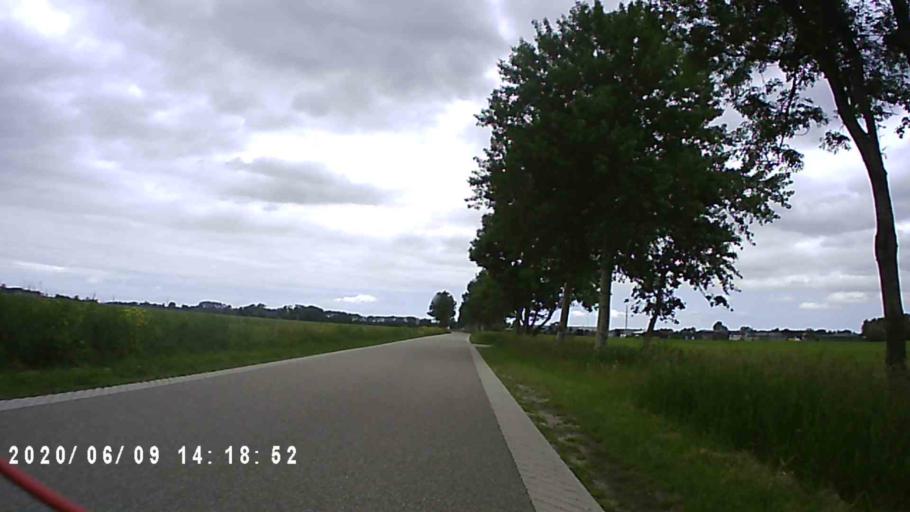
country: NL
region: Groningen
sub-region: Gemeente Bedum
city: Bedum
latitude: 53.2885
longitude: 6.5921
